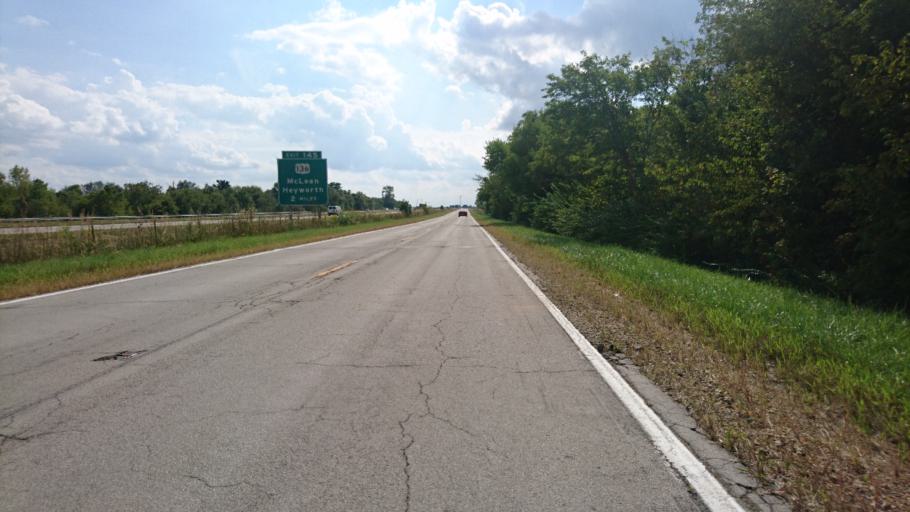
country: US
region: Illinois
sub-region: Logan County
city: Atlanta
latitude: 40.3413
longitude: -89.1381
